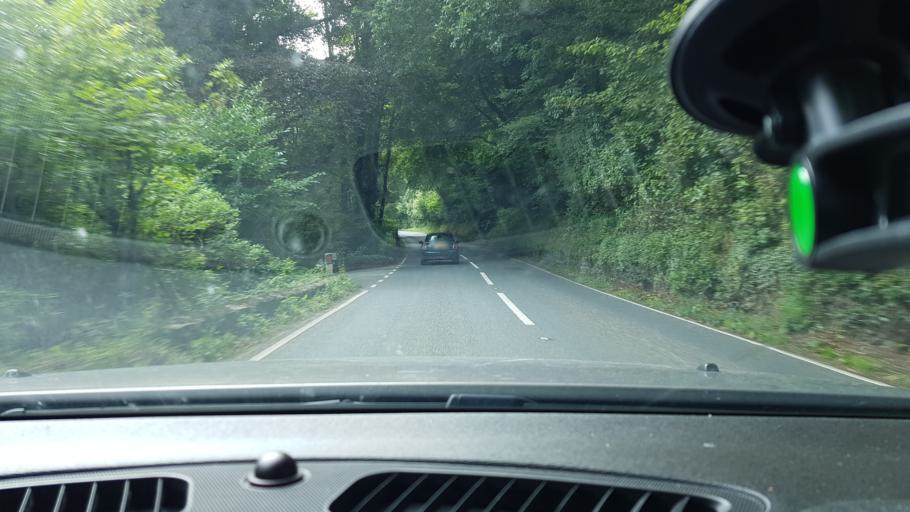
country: GB
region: England
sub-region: Cornwall
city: Helland
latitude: 50.5650
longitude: -4.7533
